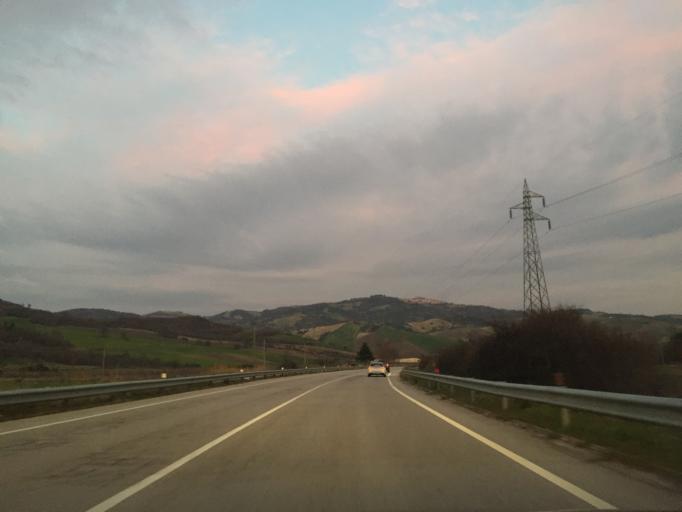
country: IT
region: Apulia
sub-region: Provincia di Foggia
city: Celenza Valfortore
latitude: 41.5264
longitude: 14.9568
